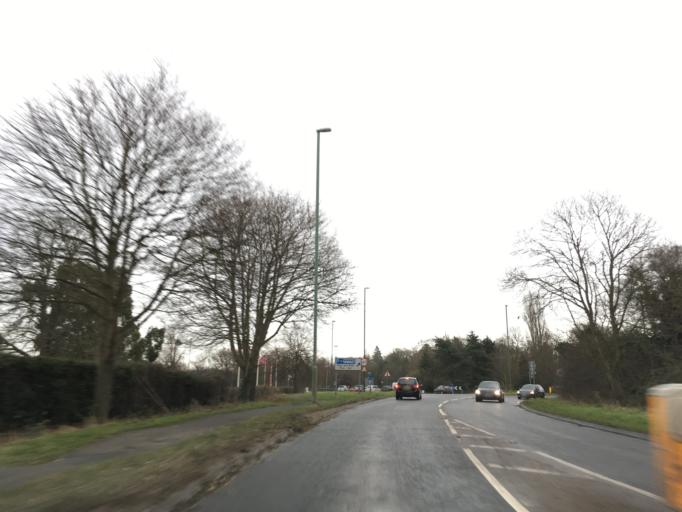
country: GB
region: England
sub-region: Gloucestershire
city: Uckington
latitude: 51.8950
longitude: -2.1317
